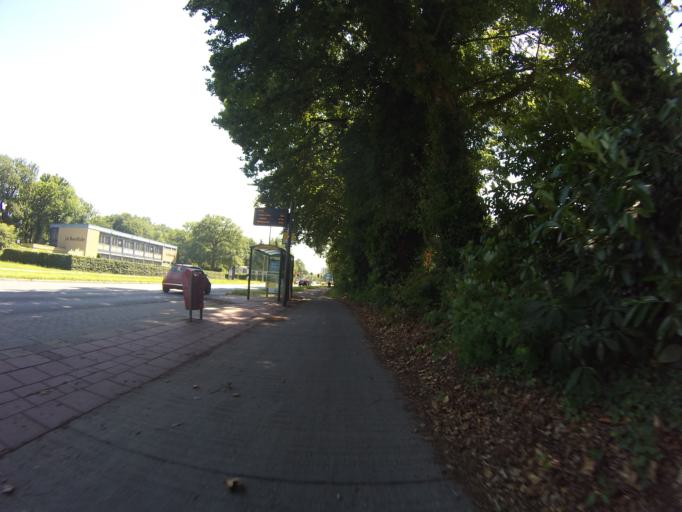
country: NL
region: Drenthe
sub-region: Gemeente Emmen
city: Emmen
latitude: 52.7814
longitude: 6.9103
